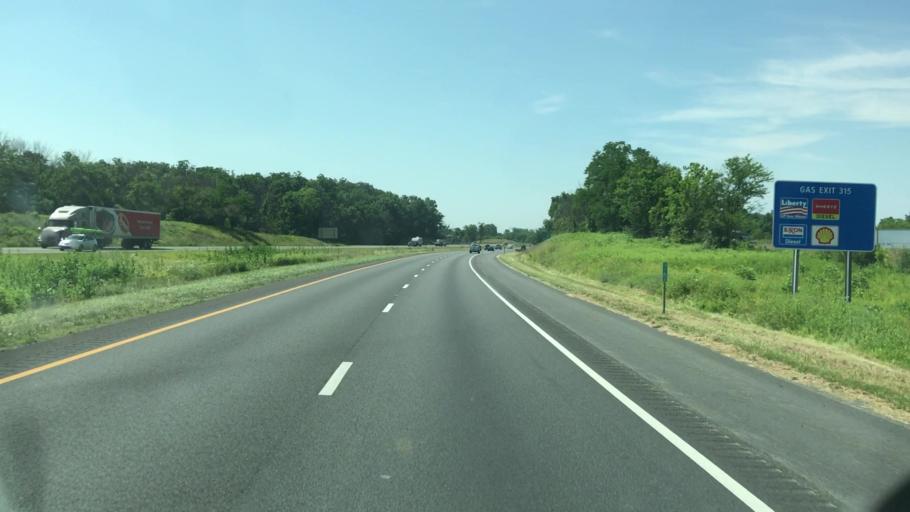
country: US
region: Virginia
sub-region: City of Winchester
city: Winchester
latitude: 39.1949
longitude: -78.1341
